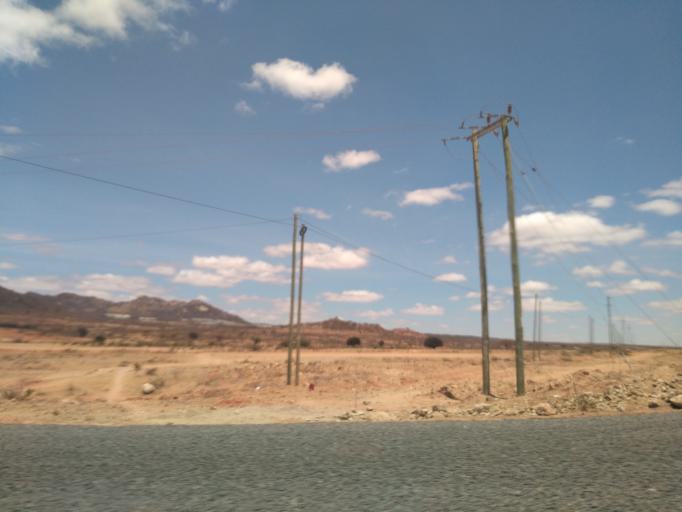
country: TZ
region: Dodoma
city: Kisasa
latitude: -6.1999
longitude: 35.8236
